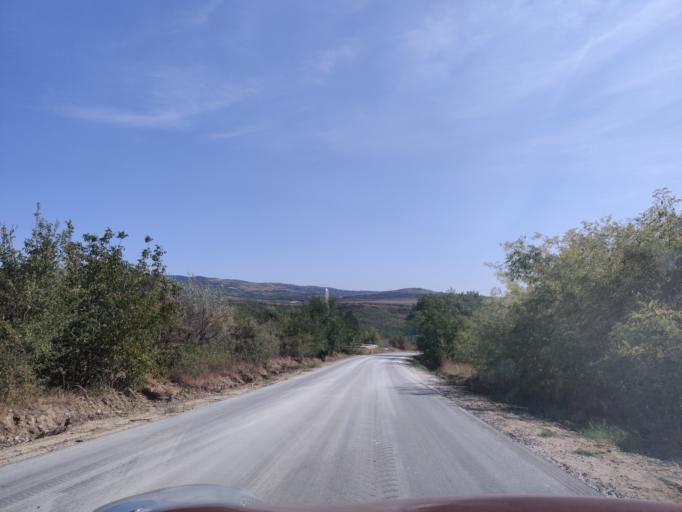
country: MD
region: Ungheni
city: Ungheni
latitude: 47.2569
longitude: 27.9945
